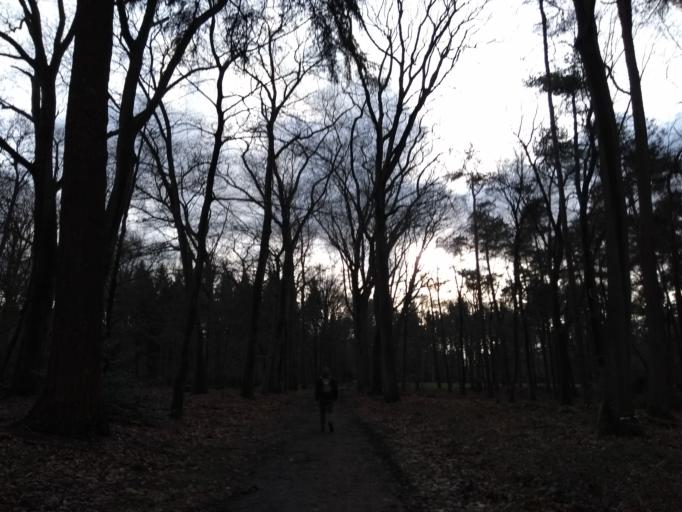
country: NL
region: Overijssel
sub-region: Gemeente Enschede
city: Enschede
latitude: 52.2586
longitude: 6.8762
